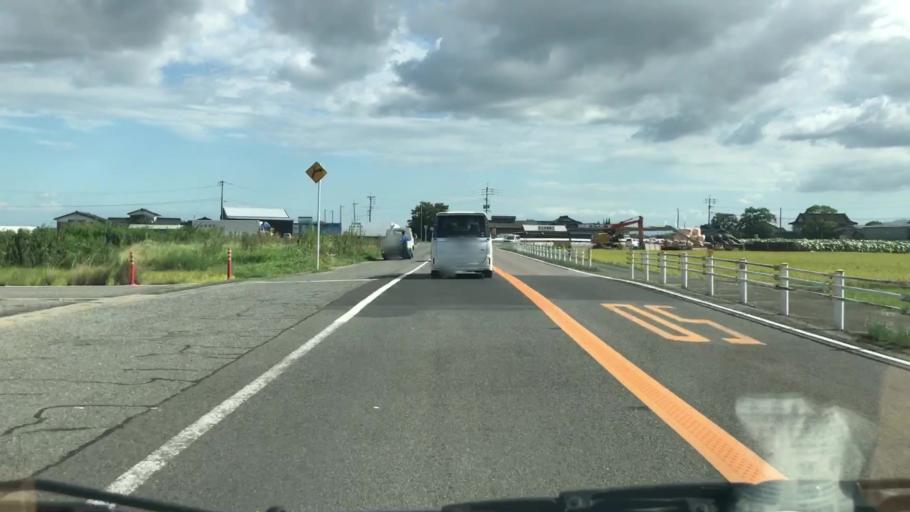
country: JP
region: Saga Prefecture
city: Kashima
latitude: 33.1714
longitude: 130.1807
